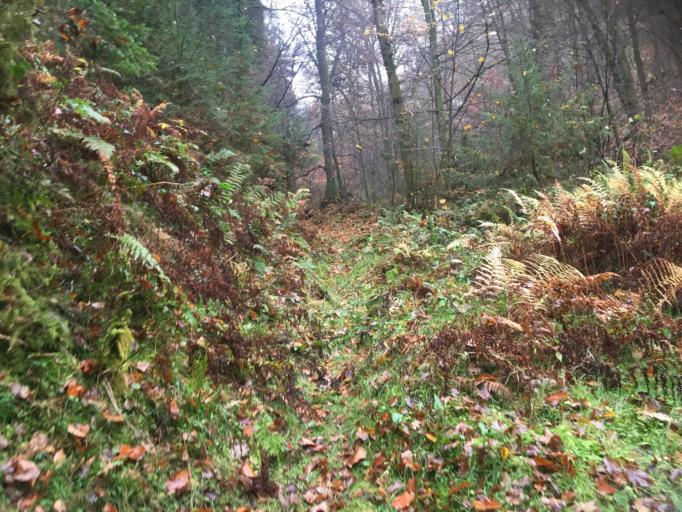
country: DE
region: Hesse
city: Hirschhorn
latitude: 49.4575
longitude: 8.8697
